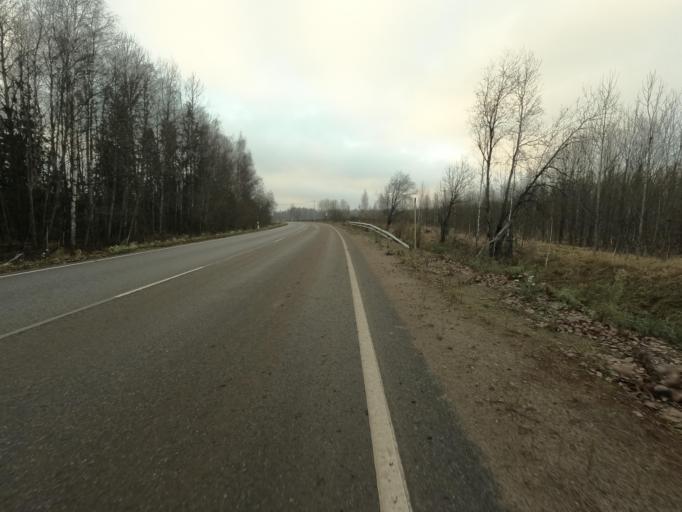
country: RU
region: Leningrad
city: Kirovsk
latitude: 59.8022
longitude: 30.9844
